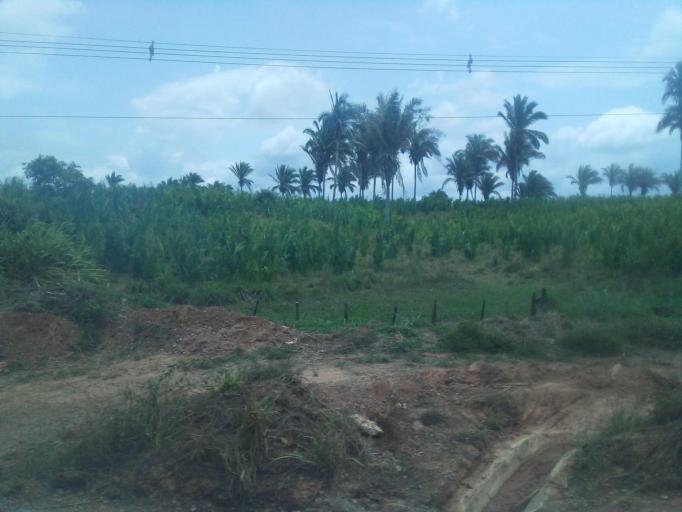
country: BR
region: Maranhao
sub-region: Santa Ines
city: Santa Ines
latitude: -3.6972
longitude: -45.6102
